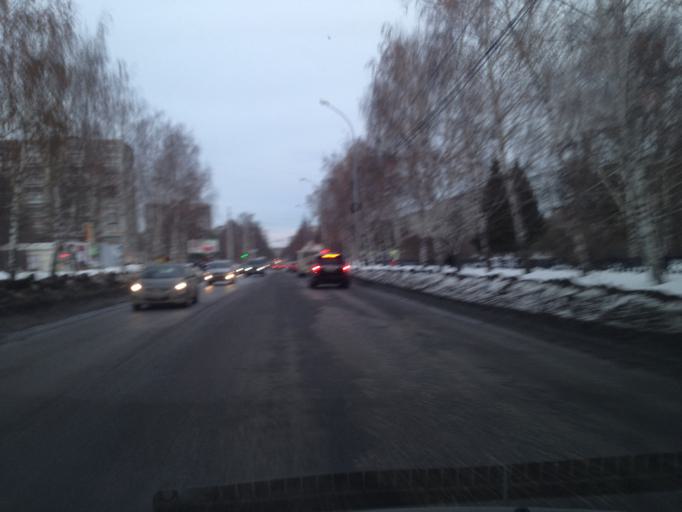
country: RU
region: Sverdlovsk
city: Sovkhoznyy
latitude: 56.8029
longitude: 60.5656
